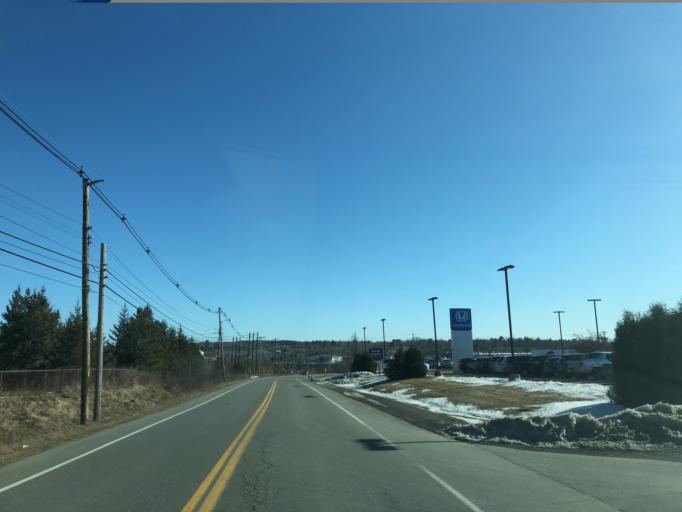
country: US
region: Maine
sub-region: Penobscot County
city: Brewer
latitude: 44.8278
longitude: -68.7464
